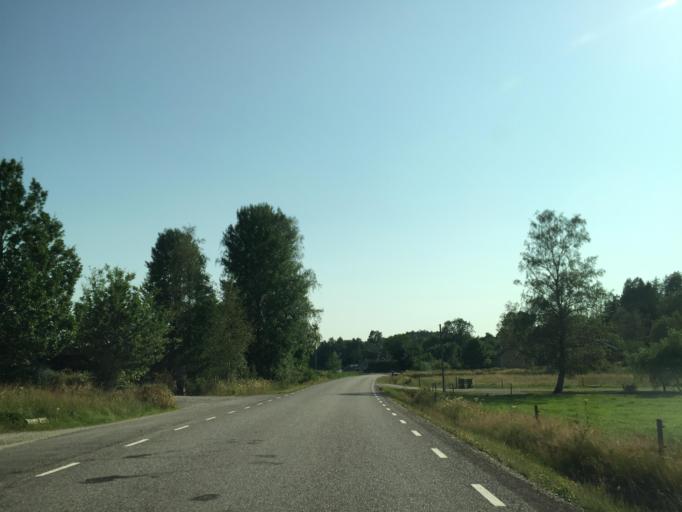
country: SE
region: Vaestra Goetaland
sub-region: Trollhattan
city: Sjuntorp
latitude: 58.2381
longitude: 12.1809
